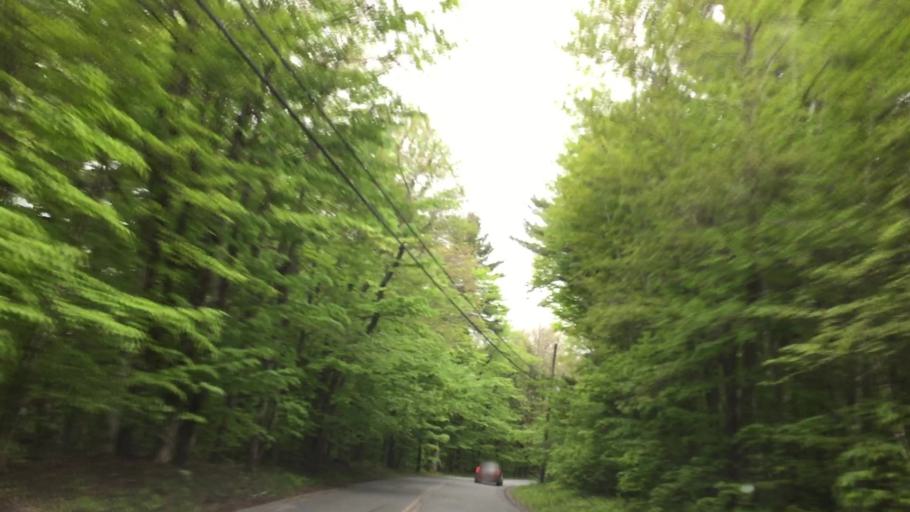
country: US
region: Massachusetts
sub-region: Berkshire County
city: Becket
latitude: 42.2816
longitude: -73.0485
